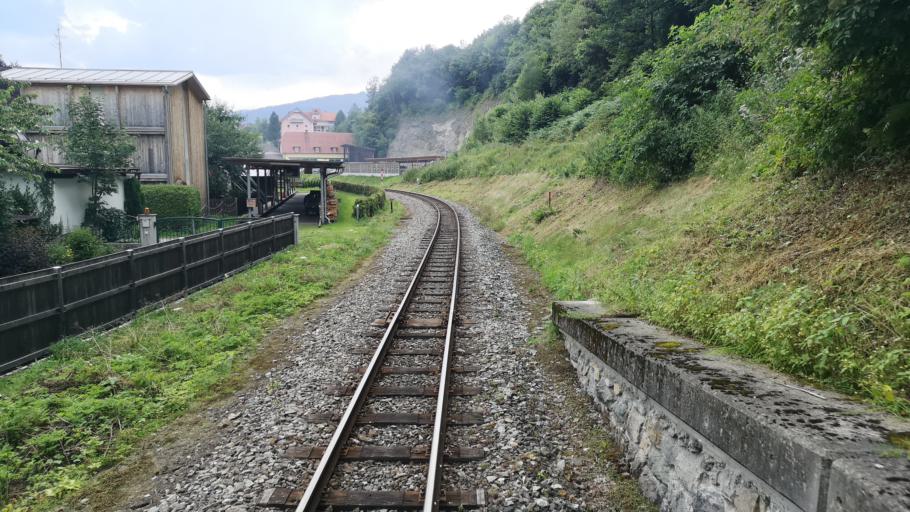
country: AT
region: Styria
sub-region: Politischer Bezirk Murau
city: Murau
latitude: 47.1083
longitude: 14.1683
